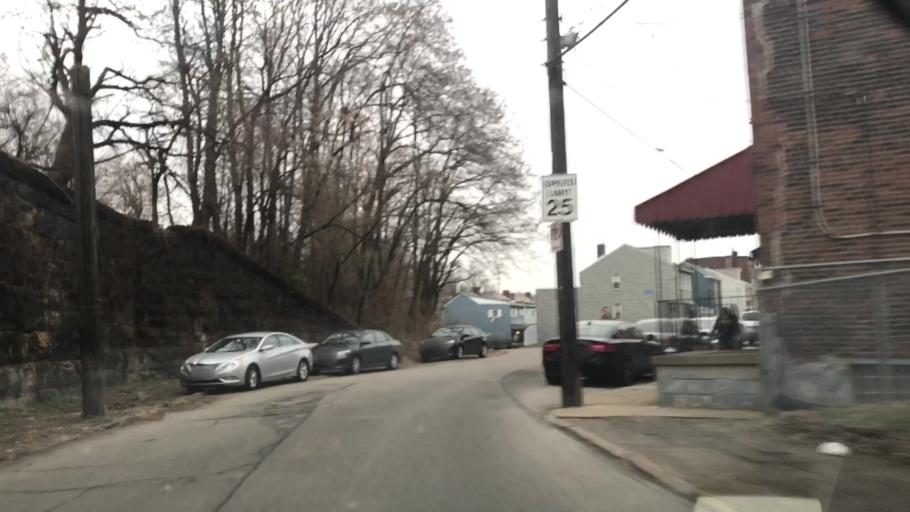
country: US
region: Pennsylvania
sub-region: Allegheny County
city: Mount Oliver
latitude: 40.4242
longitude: -79.9679
